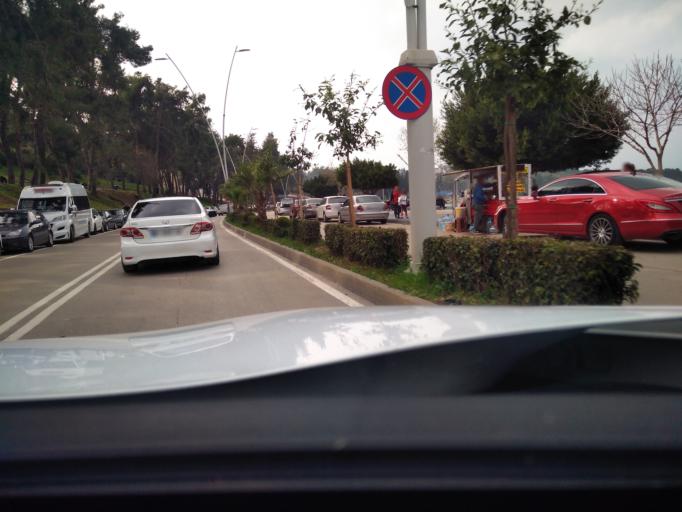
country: TR
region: Adana
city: Adana
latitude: 37.0491
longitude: 35.3099
